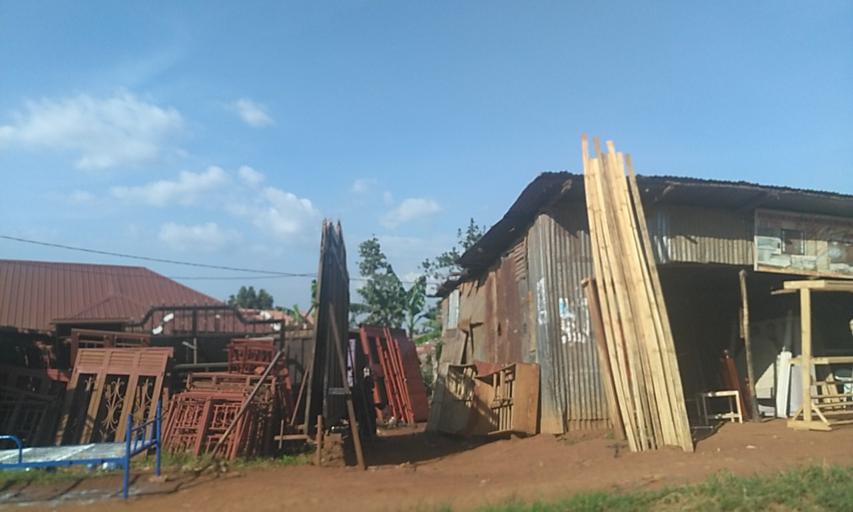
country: UG
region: Central Region
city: Kampala Central Division
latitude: 0.3256
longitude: 32.5384
